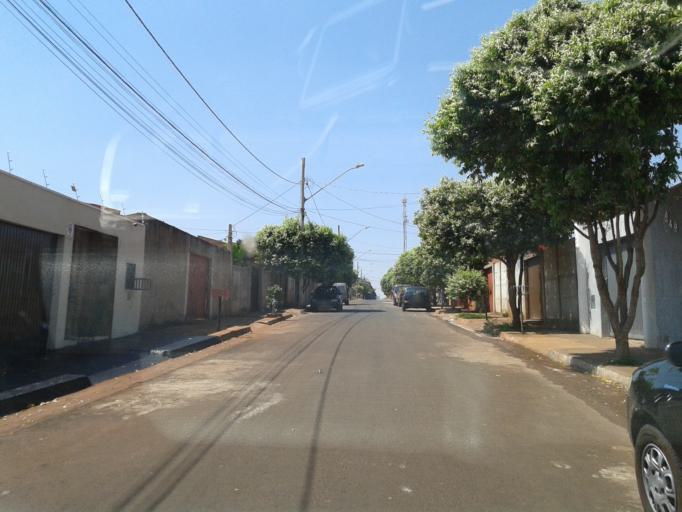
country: BR
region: Minas Gerais
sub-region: Ituiutaba
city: Ituiutaba
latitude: -18.9797
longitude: -49.4367
